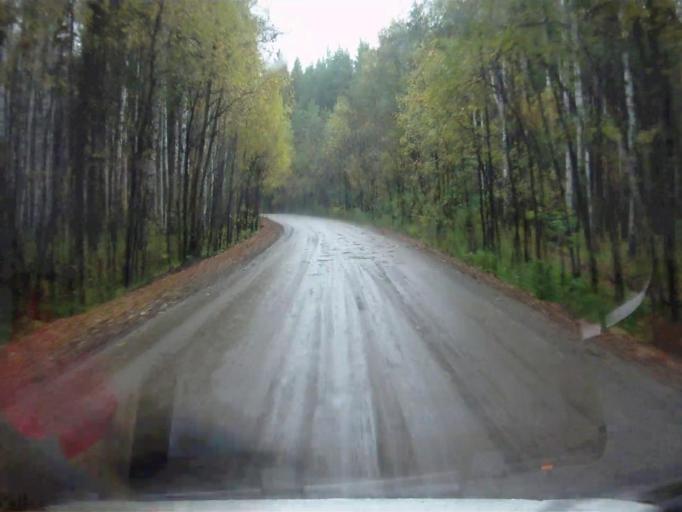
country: RU
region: Chelyabinsk
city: Kyshtym
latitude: 55.8917
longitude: 60.4654
